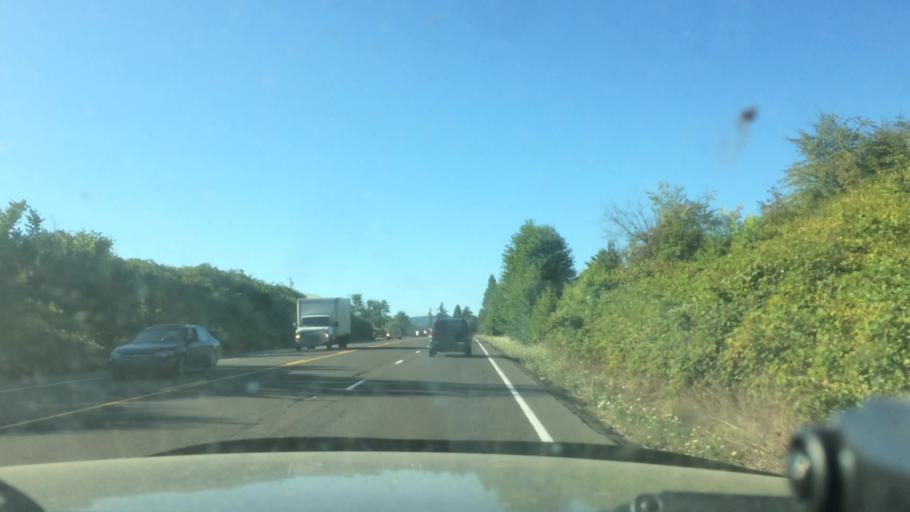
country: US
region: Oregon
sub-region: Yamhill County
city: Newberg
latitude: 45.2757
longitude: -122.9444
